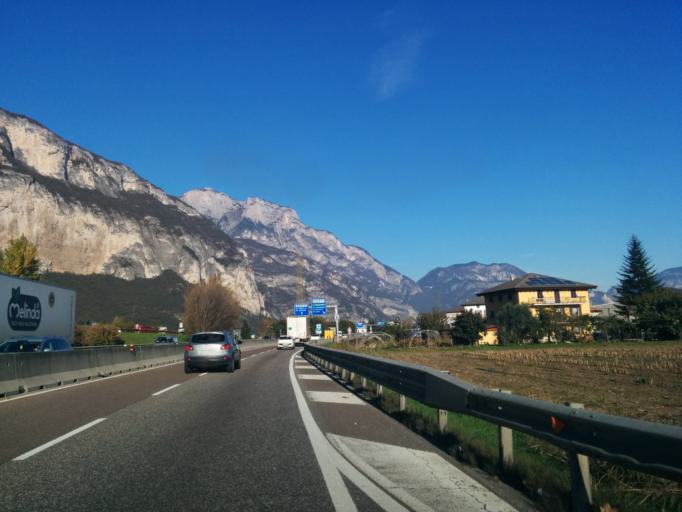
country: IT
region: Trentino-Alto Adige
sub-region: Provincia di Trento
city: Trento
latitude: 46.0878
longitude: 11.1048
